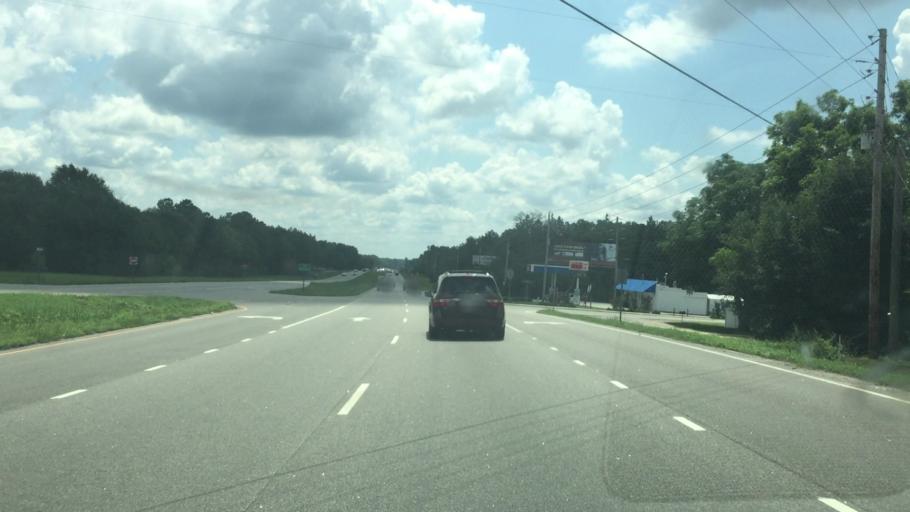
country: US
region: North Carolina
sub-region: Scotland County
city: Laurel Hill
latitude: 34.8280
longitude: -79.5923
